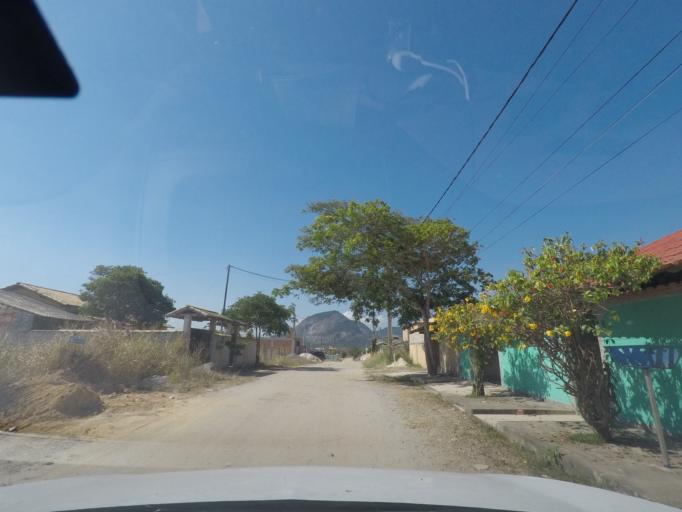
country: BR
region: Rio de Janeiro
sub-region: Marica
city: Marica
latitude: -22.9679
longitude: -42.9092
